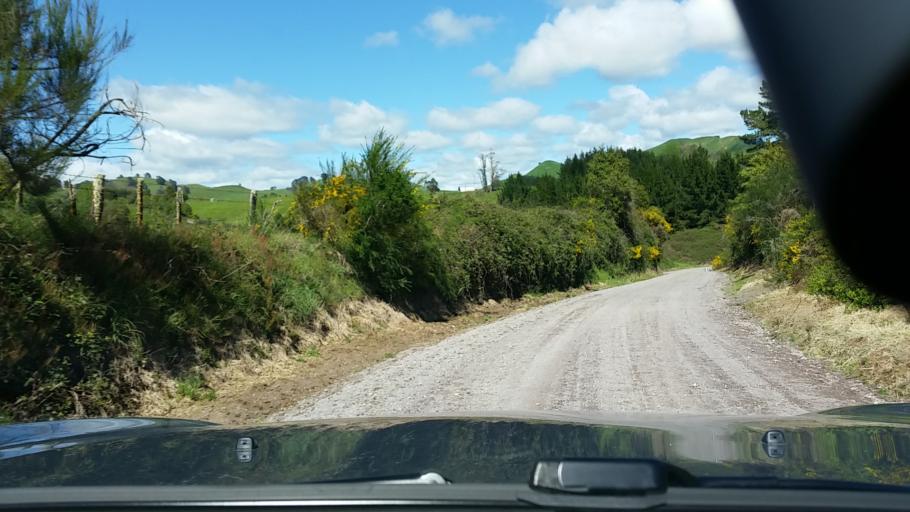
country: NZ
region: Bay of Plenty
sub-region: Rotorua District
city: Rotorua
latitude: -38.3759
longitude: 176.2047
